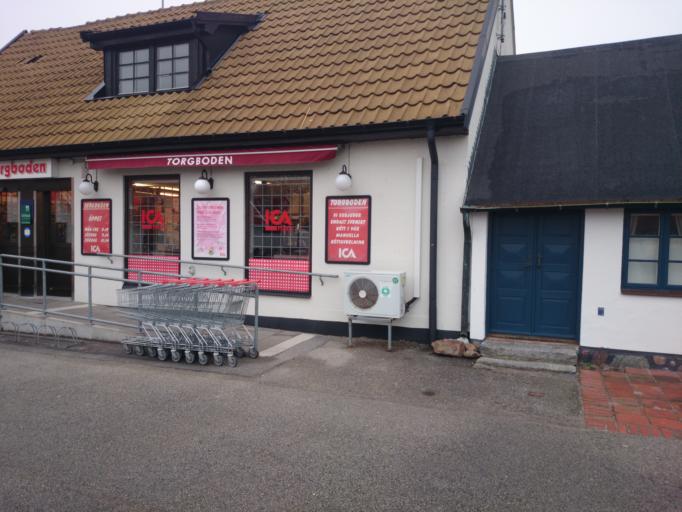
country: SE
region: Skane
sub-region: Vellinge Kommun
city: Skanor med Falsterbo
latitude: 55.3911
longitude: 12.8343
